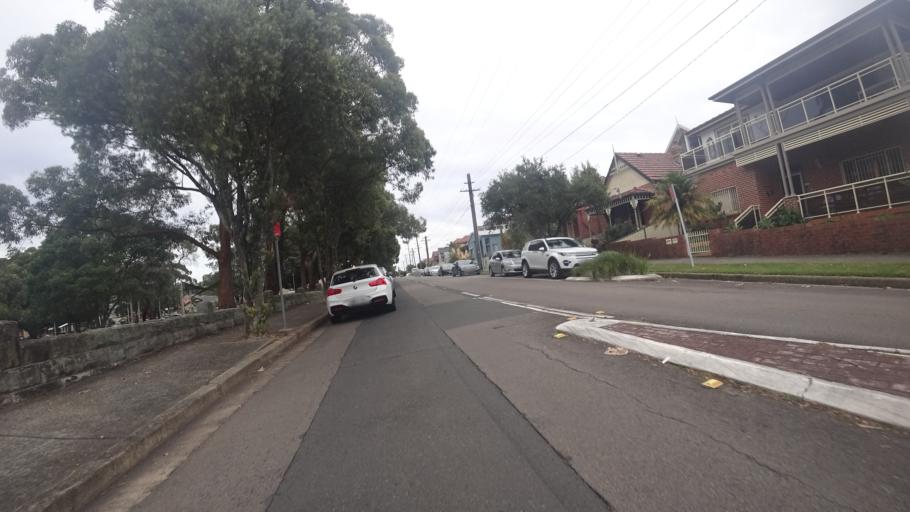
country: AU
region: New South Wales
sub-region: Rockdale
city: Bardwell Valley
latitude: -33.9344
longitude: 151.1418
